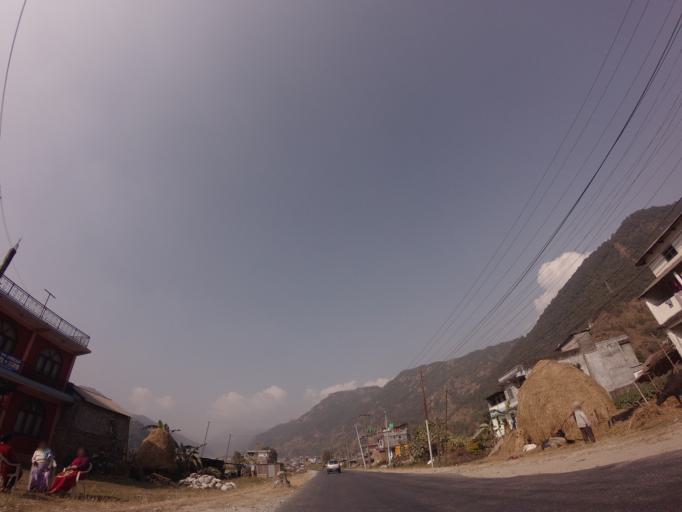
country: NP
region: Western Region
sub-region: Gandaki Zone
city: Pokhara
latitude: 28.2812
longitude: 83.9275
